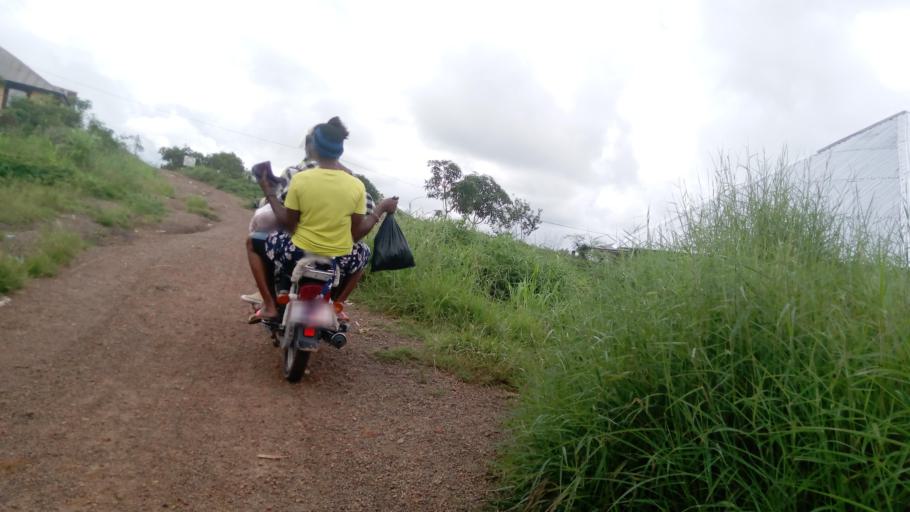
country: SL
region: Northern Province
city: Makeni
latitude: 8.8955
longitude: -12.0248
